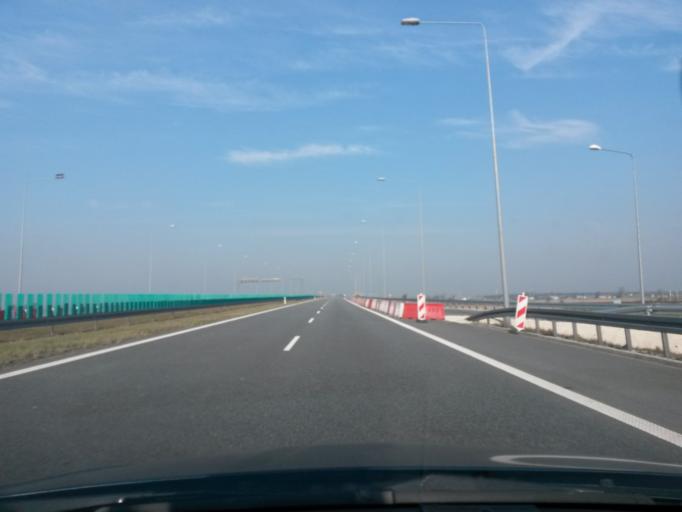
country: PL
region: Lodz Voivodeship
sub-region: Powiat kutnowski
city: Krzyzanow
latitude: 52.2262
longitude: 19.4638
